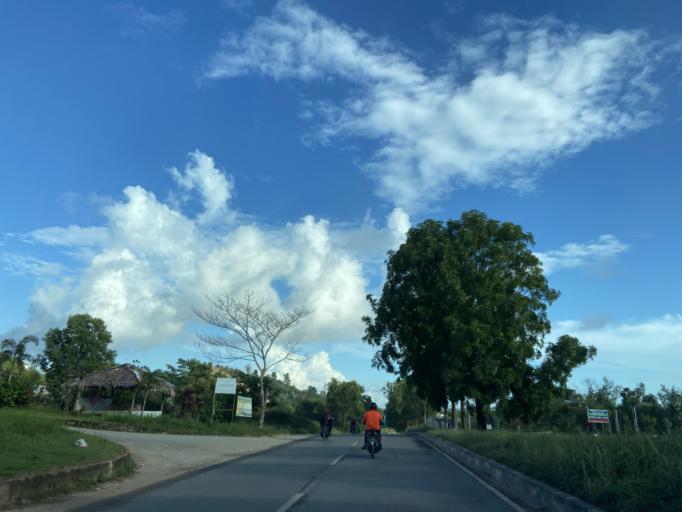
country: SG
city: Singapore
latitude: 1.0335
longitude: 104.0000
